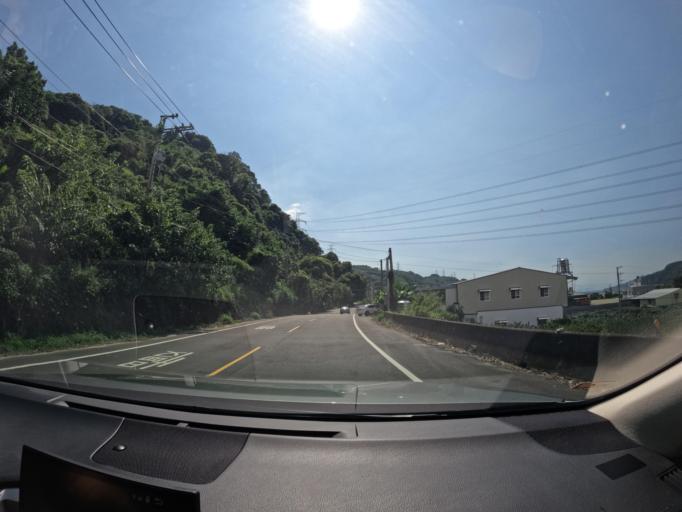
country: TW
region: Taiwan
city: Fengyuan
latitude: 24.3150
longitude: 120.7763
